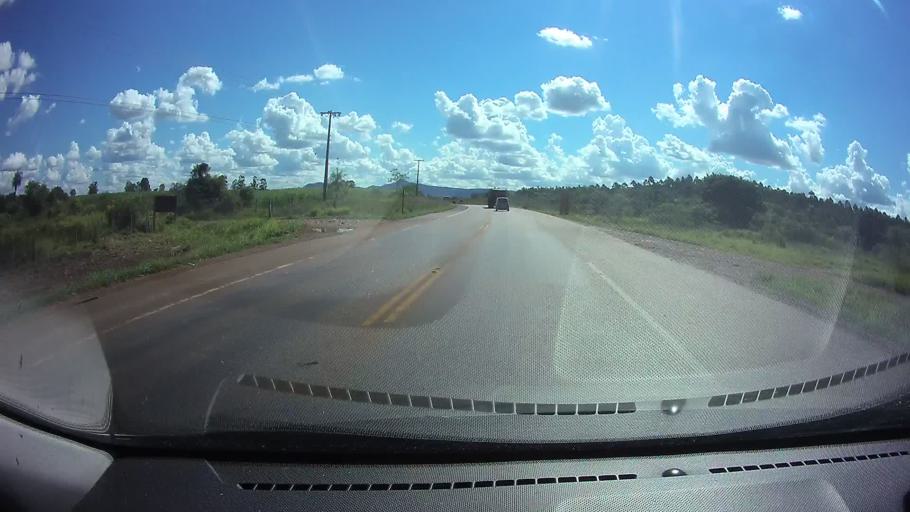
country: PY
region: Guaira
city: Coronel Martinez
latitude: -25.7587
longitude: -56.7074
